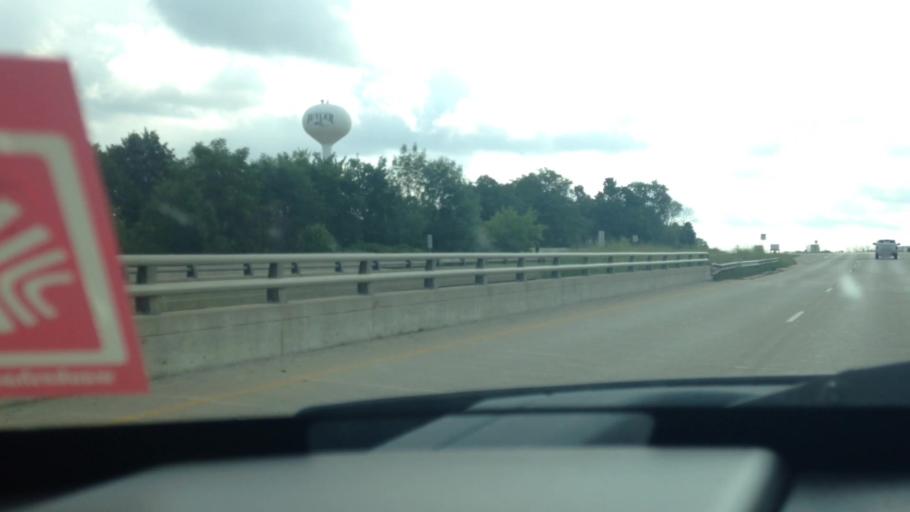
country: US
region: Wisconsin
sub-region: Waukesha County
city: Butler
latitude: 43.1181
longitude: -88.0756
